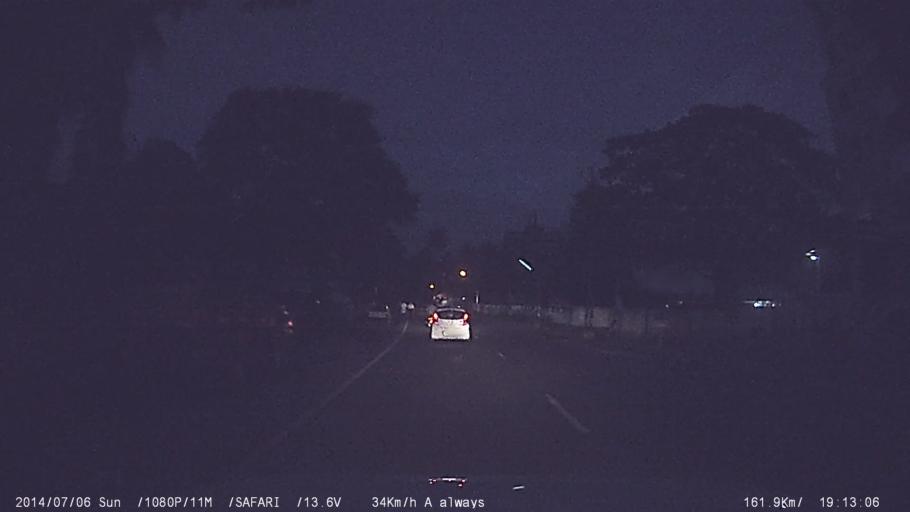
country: IN
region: Kerala
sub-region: Palakkad district
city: Palakkad
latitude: 10.7656
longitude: 76.6597
